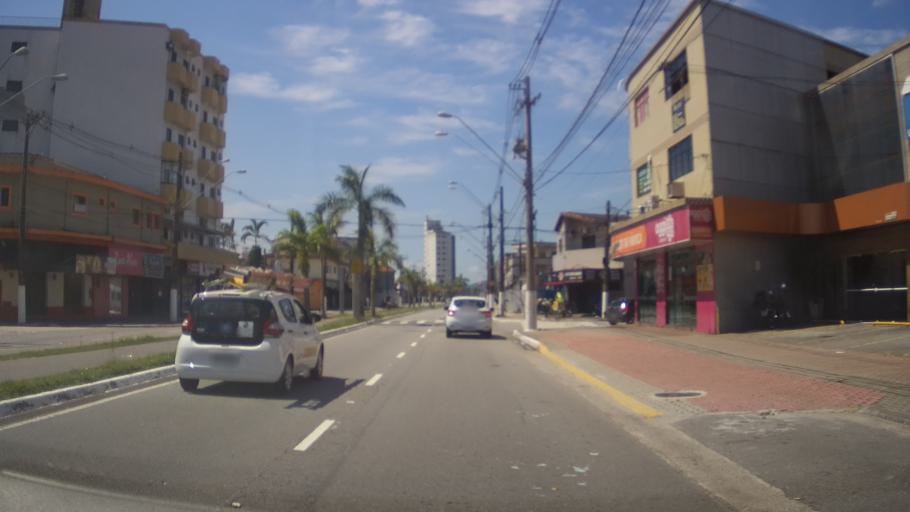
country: BR
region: Sao Paulo
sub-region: Praia Grande
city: Praia Grande
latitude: -24.0236
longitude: -46.4730
